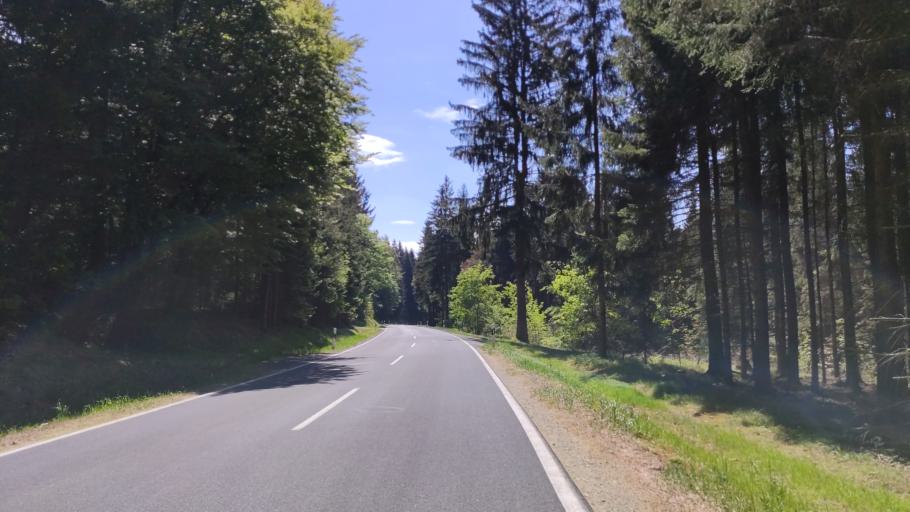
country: DE
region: Bavaria
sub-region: Upper Franconia
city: Reichenbach
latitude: 50.4419
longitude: 11.4150
